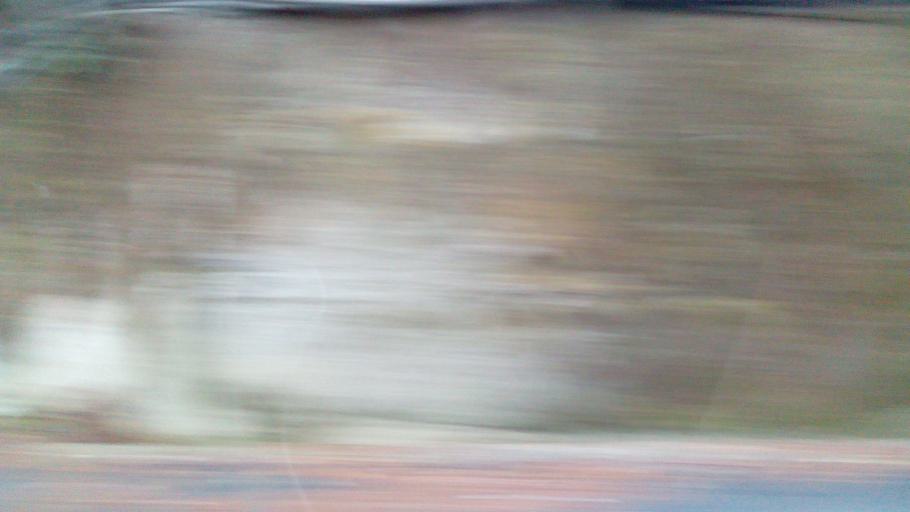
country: TW
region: Taiwan
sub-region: Hualien
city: Hualian
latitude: 24.3292
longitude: 121.3095
